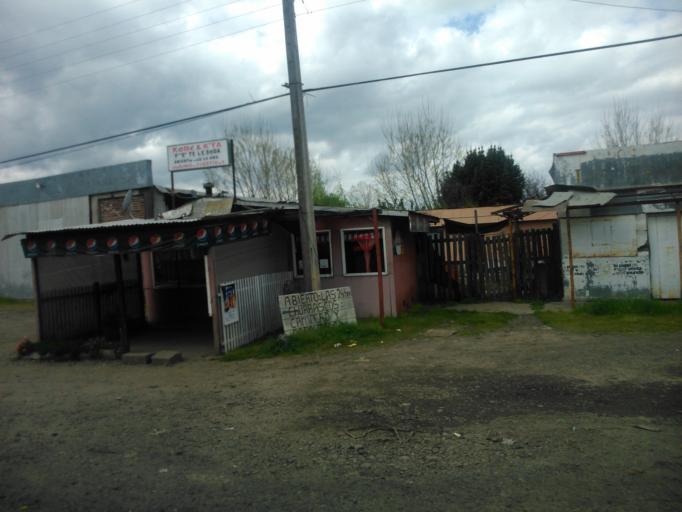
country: CL
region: Biobio
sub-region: Provincia de Nuble
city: Bulnes
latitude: -36.7542
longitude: -72.2911
